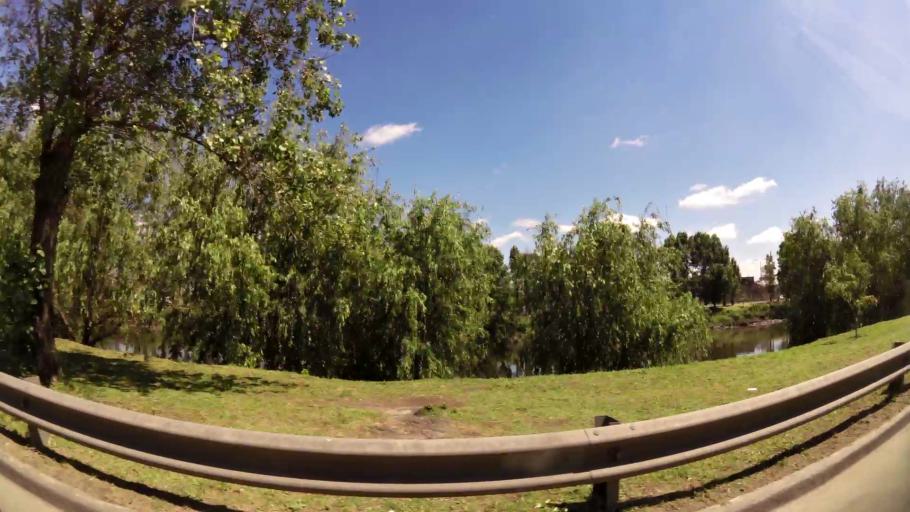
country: AR
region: Buenos Aires
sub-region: Partido de Lanus
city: Lanus
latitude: -34.6649
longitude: -58.4262
